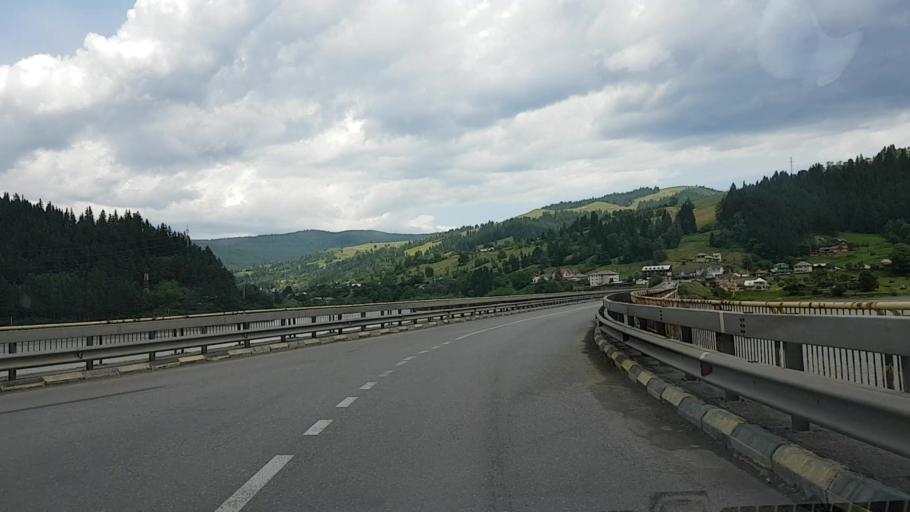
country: RO
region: Neamt
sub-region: Comuna Poiana Teiului
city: Poiana Teiului
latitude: 47.0893
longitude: 25.9613
